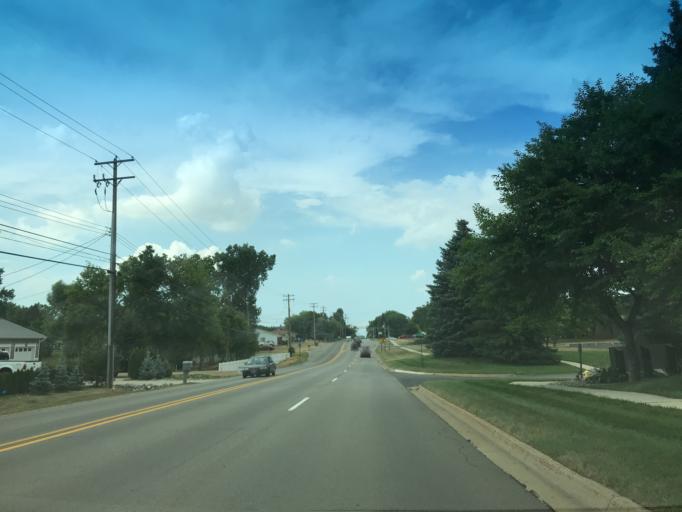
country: US
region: Michigan
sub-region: Eaton County
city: Waverly
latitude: 42.7240
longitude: -84.6620
